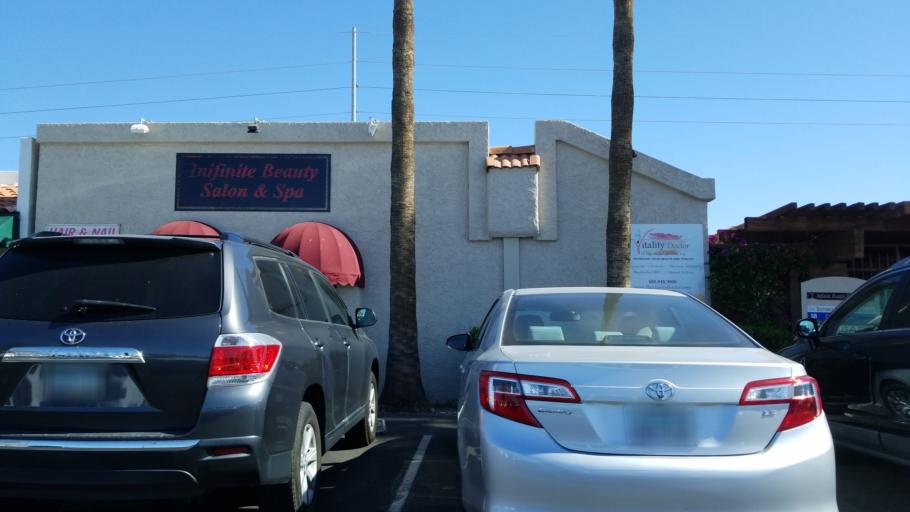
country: US
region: Arizona
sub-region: Maricopa County
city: Paradise Valley
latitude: 33.5811
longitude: -111.9243
